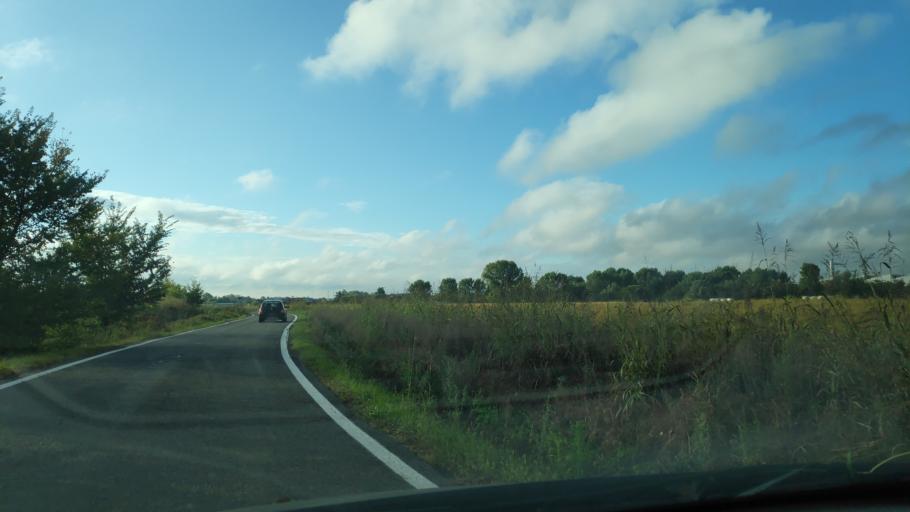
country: IT
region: Lombardy
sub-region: Citta metropolitana di Milano
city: Fizzonasco
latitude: 45.3822
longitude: 9.1910
